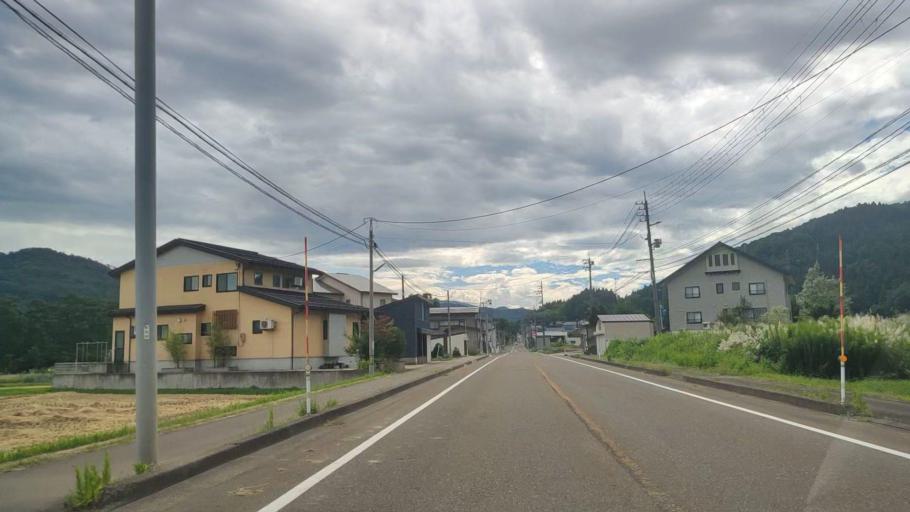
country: JP
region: Niigata
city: Arai
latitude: 37.0042
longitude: 138.2627
